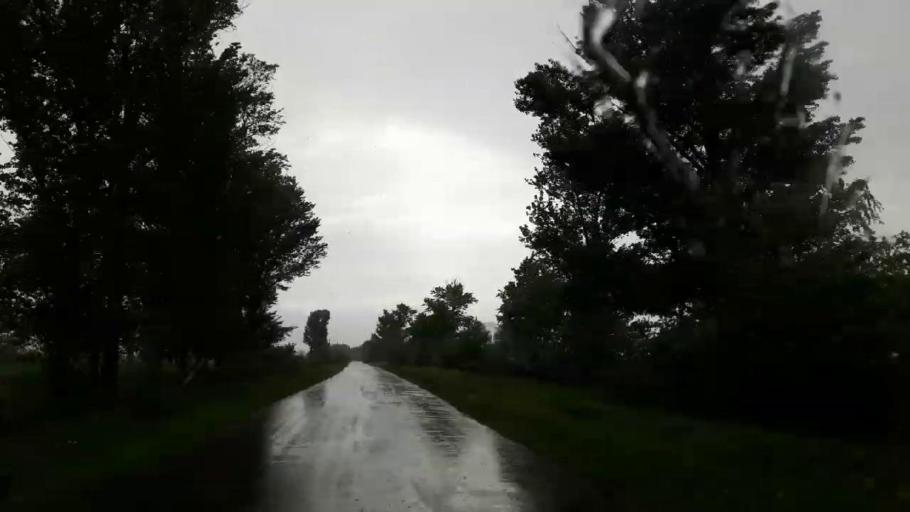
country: GE
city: Agara
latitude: 42.0134
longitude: 43.7962
